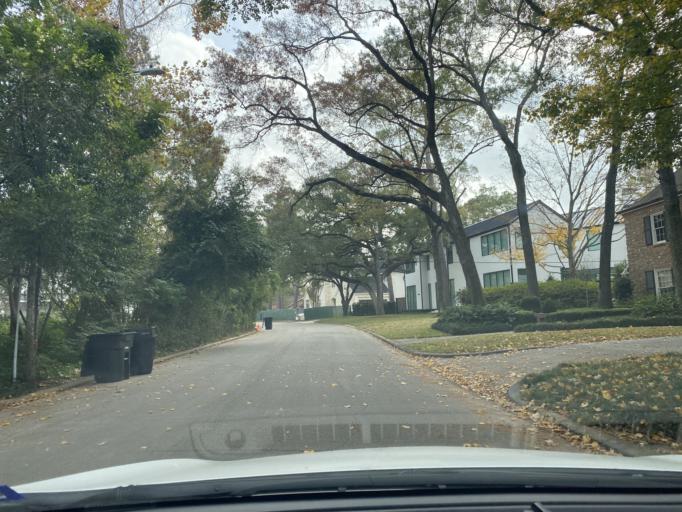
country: US
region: Texas
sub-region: Harris County
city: Hunters Creek Village
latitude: 29.7650
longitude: -95.4614
